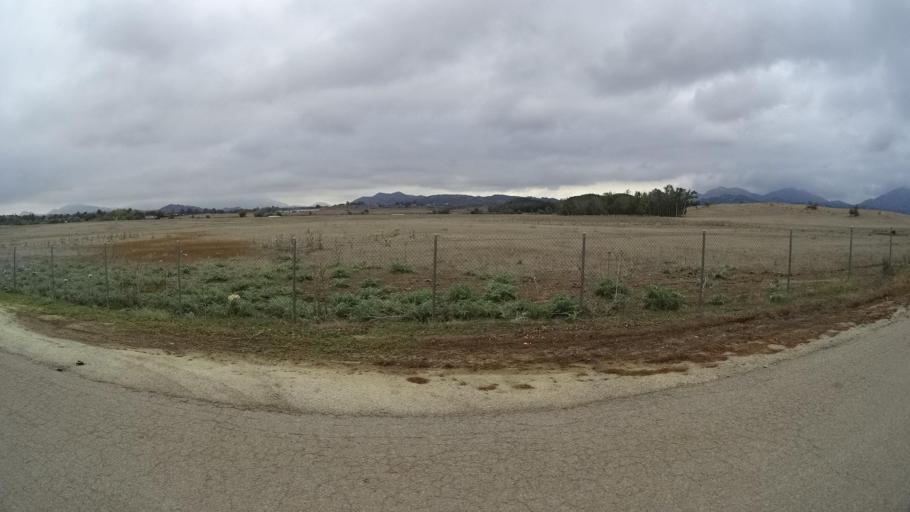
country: US
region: California
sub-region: San Diego County
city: Ramona
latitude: 33.0359
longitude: -116.9092
